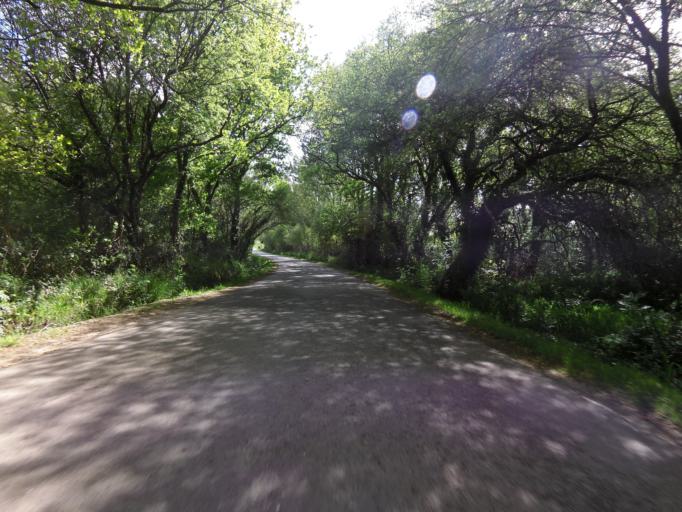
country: FR
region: Brittany
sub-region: Departement du Morbihan
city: Plougoumelen
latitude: 47.6489
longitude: -2.8953
